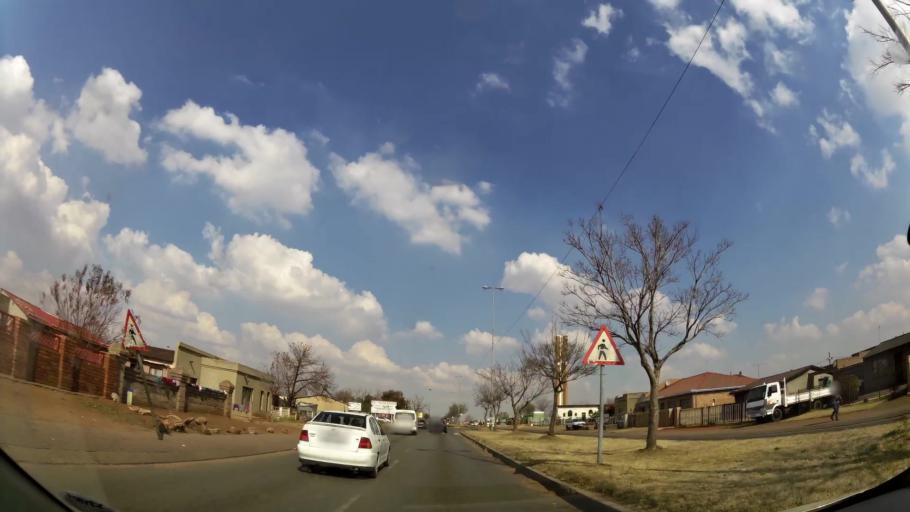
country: ZA
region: Gauteng
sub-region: Ekurhuleni Metropolitan Municipality
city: Germiston
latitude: -26.3326
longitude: 28.1618
